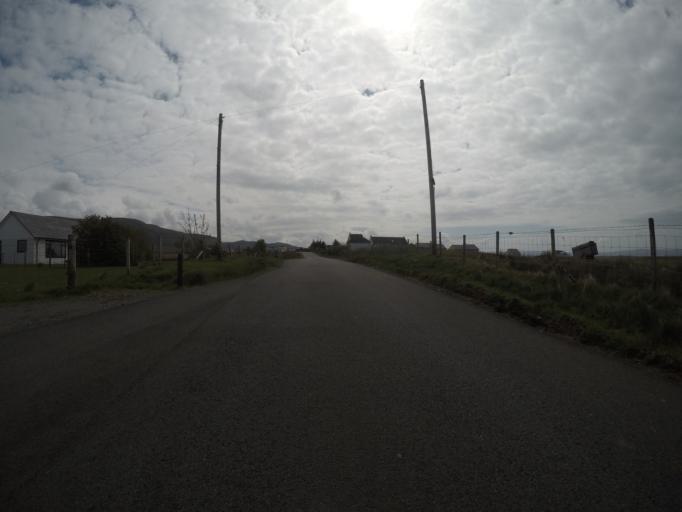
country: GB
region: Scotland
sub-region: Highland
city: Portree
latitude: 57.6483
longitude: -6.3802
